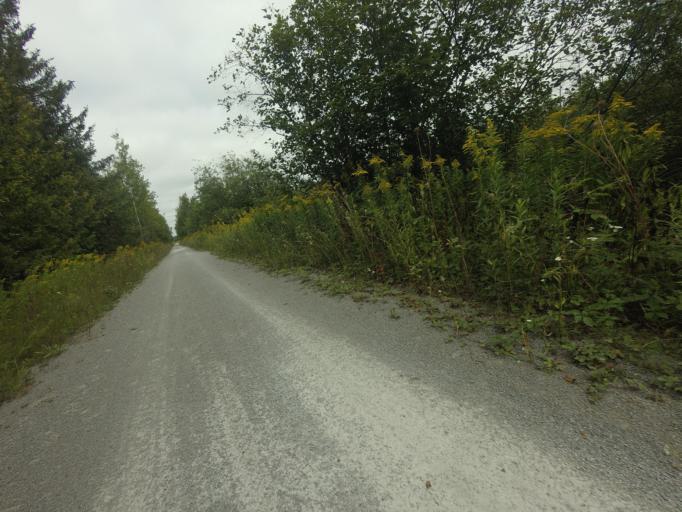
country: CA
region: Ontario
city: Uxbridge
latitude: 44.2184
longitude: -79.0623
